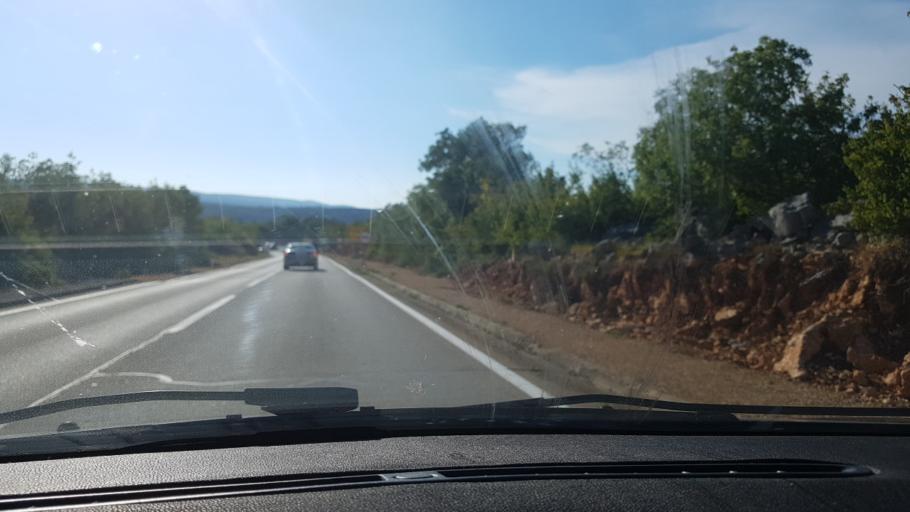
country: HR
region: Zadarska
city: Posedarje
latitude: 44.2296
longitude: 15.5335
